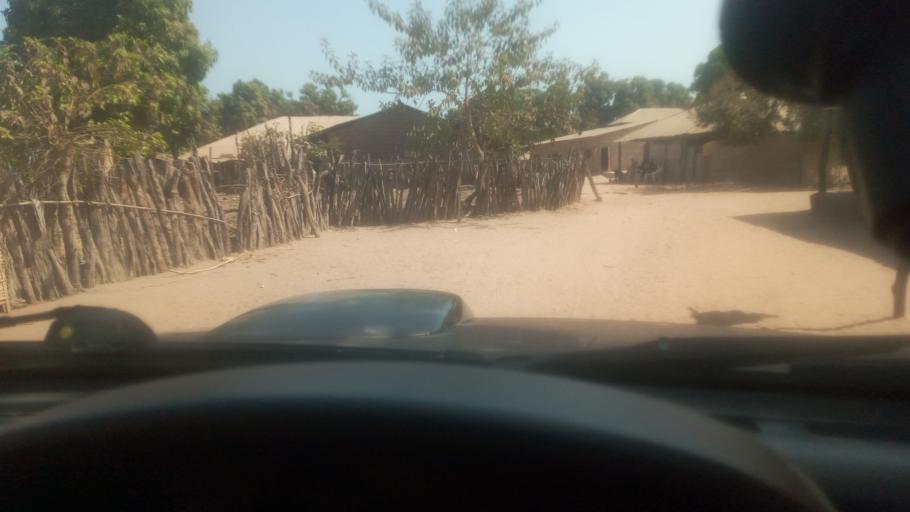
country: GW
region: Oio
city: Farim
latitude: 12.4969
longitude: -15.4054
